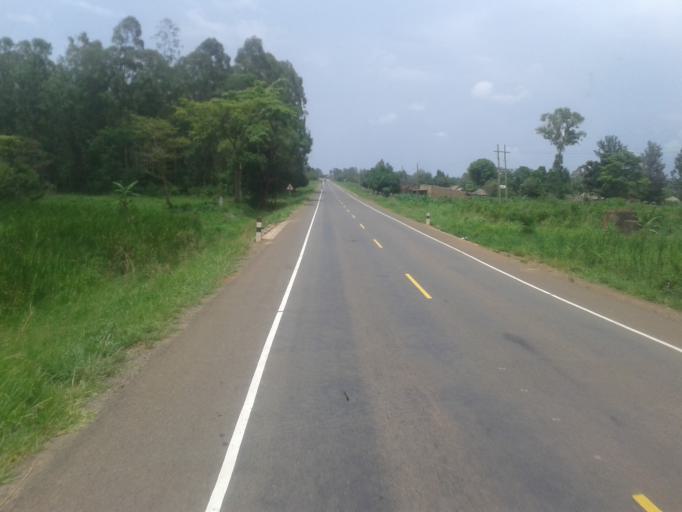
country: UG
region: Western Region
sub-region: Kiryandongo District
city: Kiryandongo
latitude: 1.9244
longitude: 32.1070
